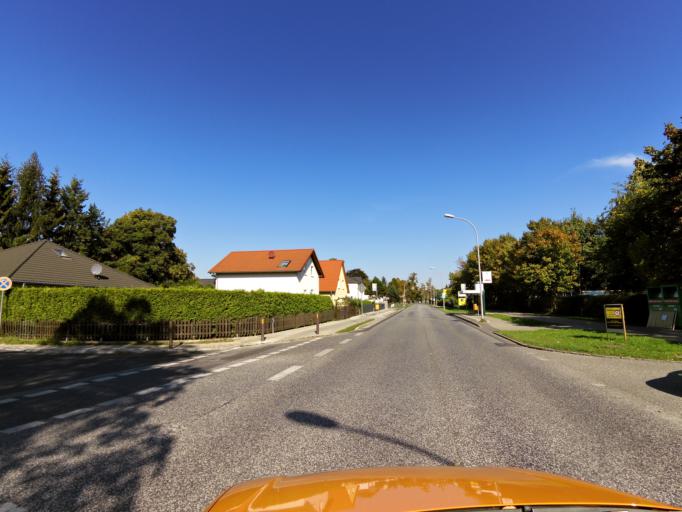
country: DE
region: Brandenburg
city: Stahnsdorf
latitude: 52.3786
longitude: 13.2080
